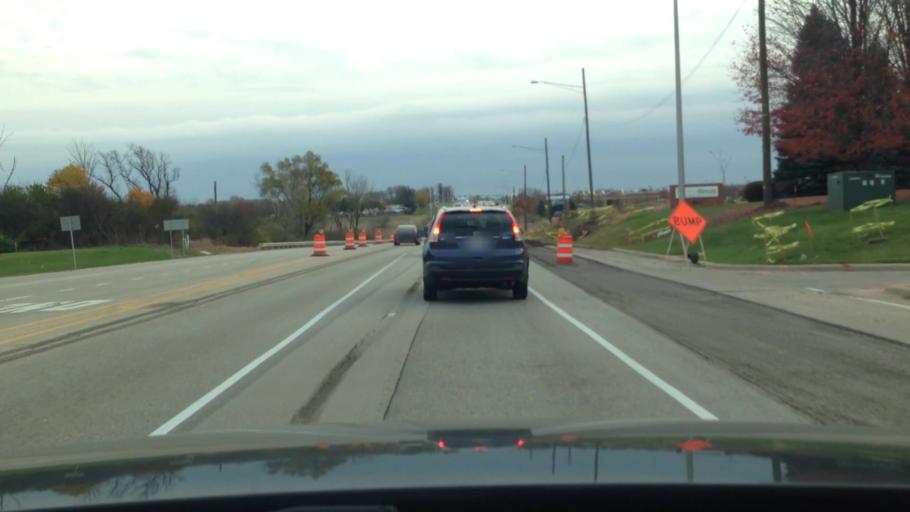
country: US
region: Illinois
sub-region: McHenry County
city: Lake in the Hills
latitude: 42.1673
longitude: -88.3354
